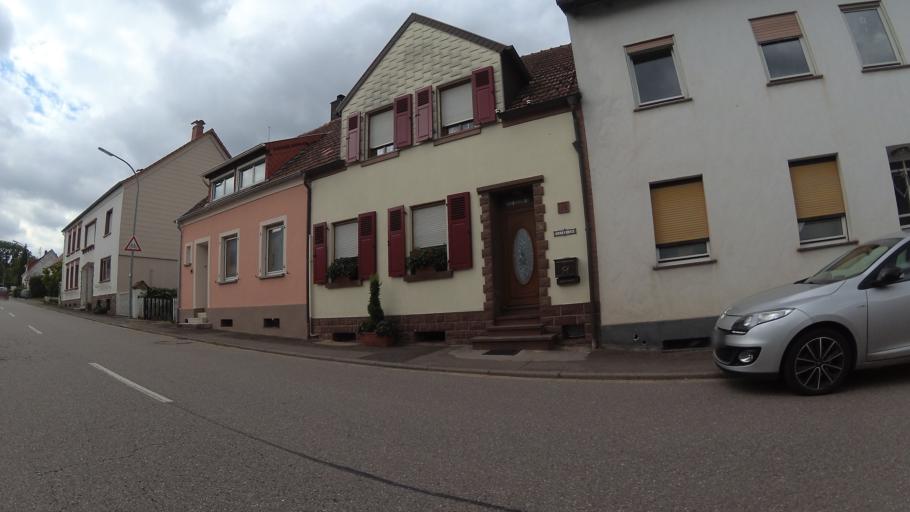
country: FR
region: Lorraine
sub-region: Departement de la Moselle
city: Sarreinsming
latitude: 49.1455
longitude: 7.1108
